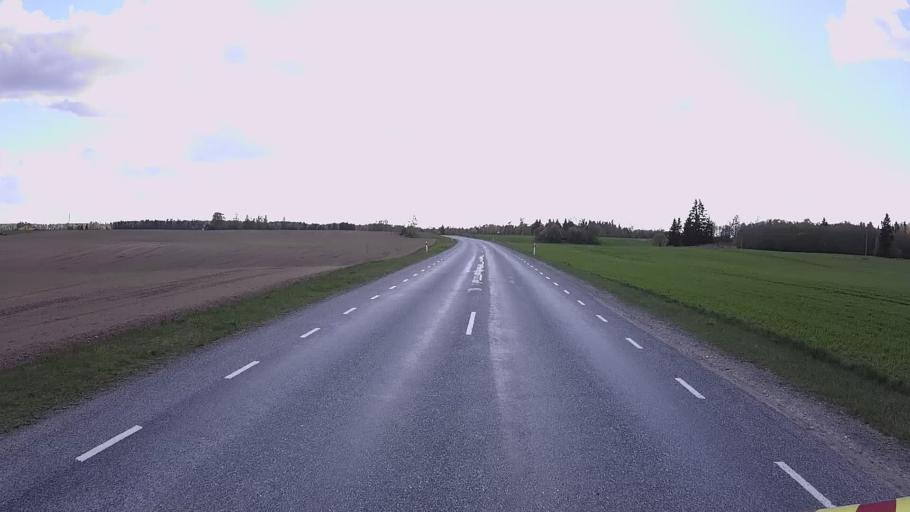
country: EE
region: Jogevamaa
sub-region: Poltsamaa linn
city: Poltsamaa
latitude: 58.6855
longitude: 26.0894
